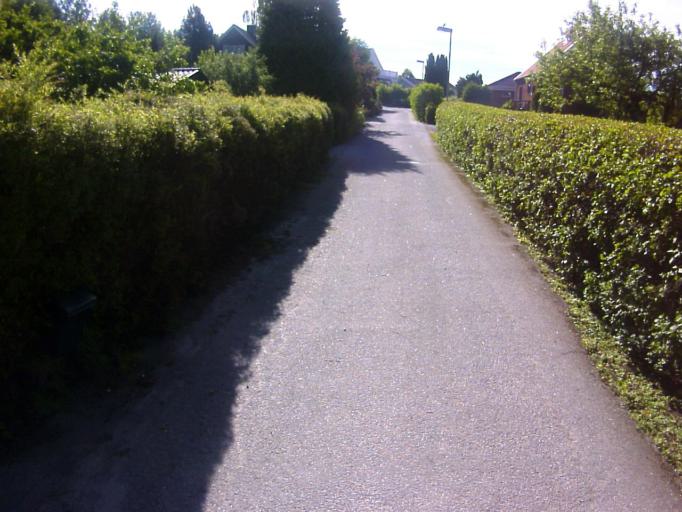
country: SE
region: Soedermanland
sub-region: Eskilstuna Kommun
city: Skogstorp
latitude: 59.3190
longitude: 16.4645
